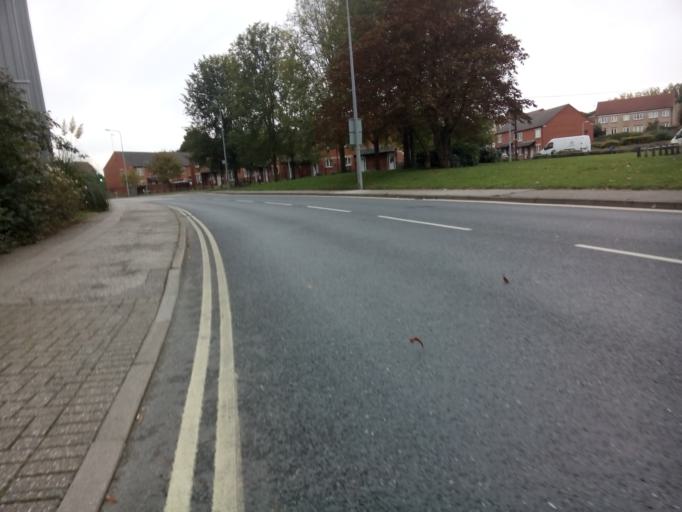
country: GB
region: England
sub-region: Suffolk
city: Ipswich
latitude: 52.0450
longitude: 1.1551
